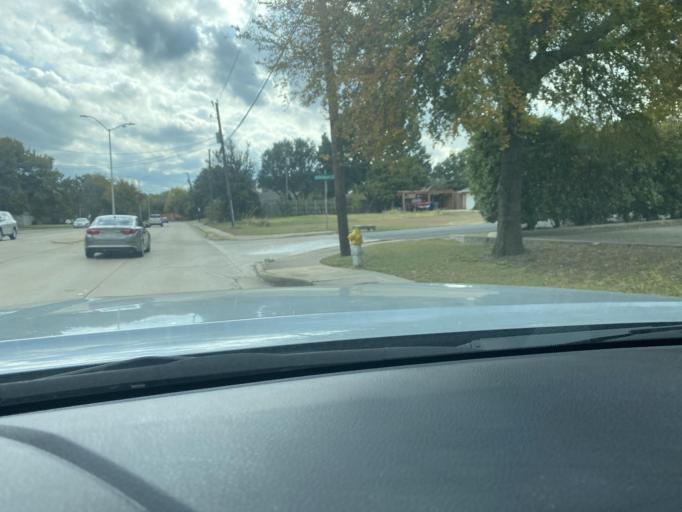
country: US
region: Texas
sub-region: Dallas County
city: Addison
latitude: 32.9921
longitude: -96.7847
